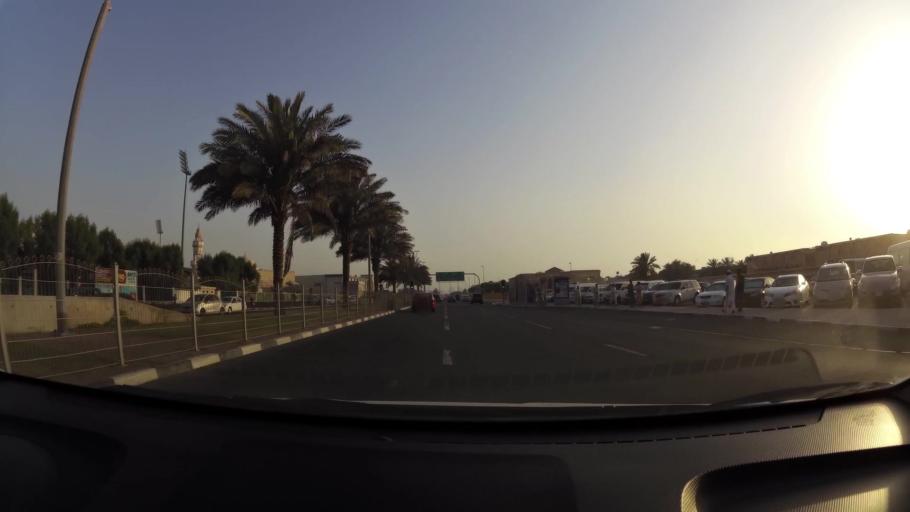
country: AE
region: Ash Shariqah
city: Sharjah
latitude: 25.2928
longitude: 55.3480
